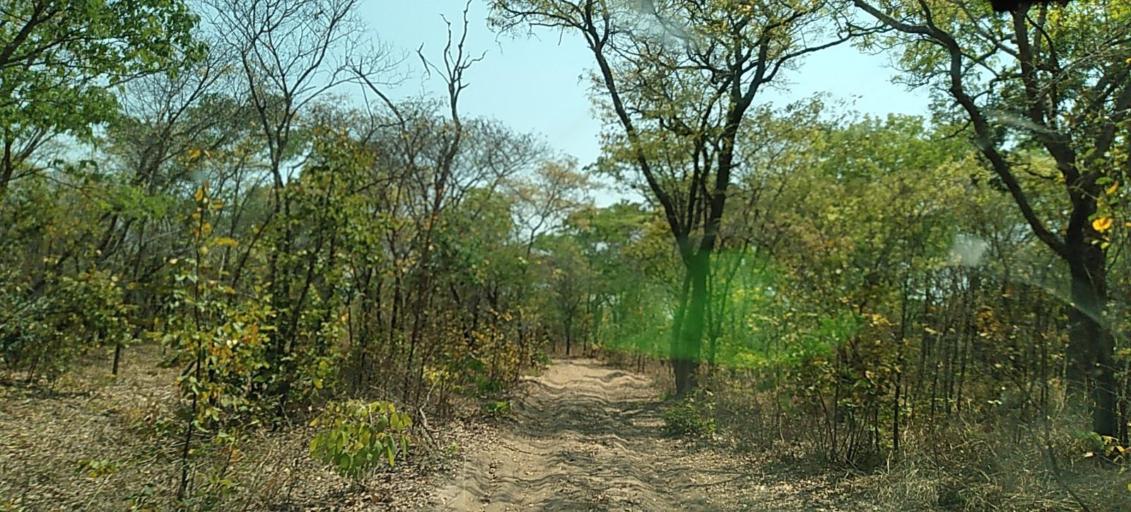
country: ZM
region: North-Western
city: Kalengwa
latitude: -13.1138
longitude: 24.6902
